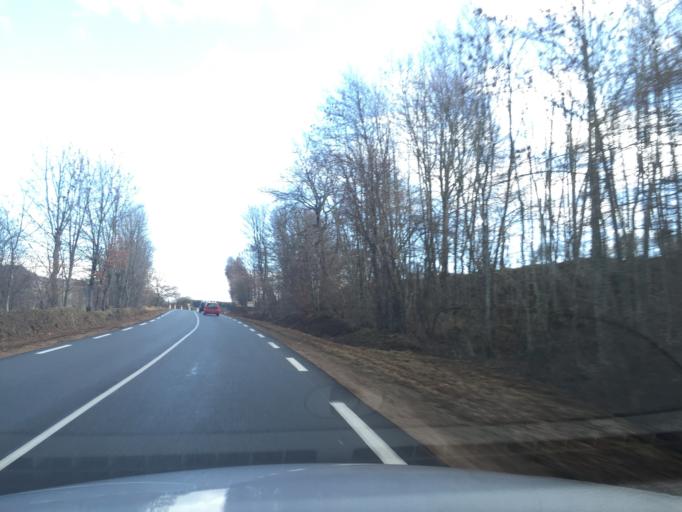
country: FR
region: Auvergne
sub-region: Departement du Puy-de-Dome
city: Saint-Ours
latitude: 45.8196
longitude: 2.9258
